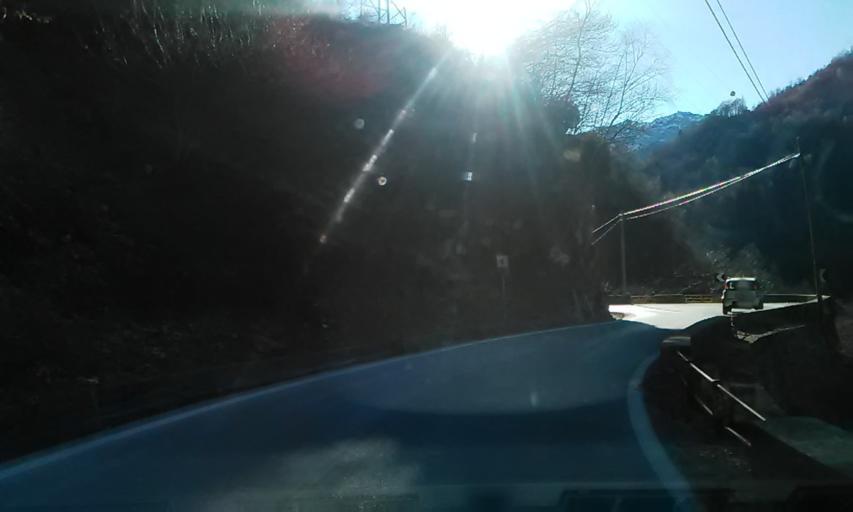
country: IT
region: Piedmont
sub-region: Provincia di Vercelli
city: Boccioleto
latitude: 45.8365
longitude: 8.0883
